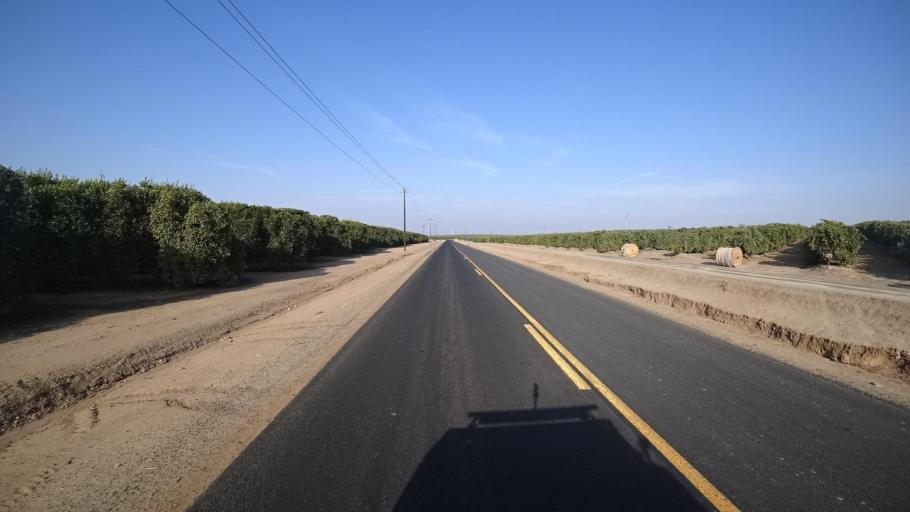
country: US
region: California
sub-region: Kern County
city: McFarland
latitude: 35.6721
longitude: -119.1317
